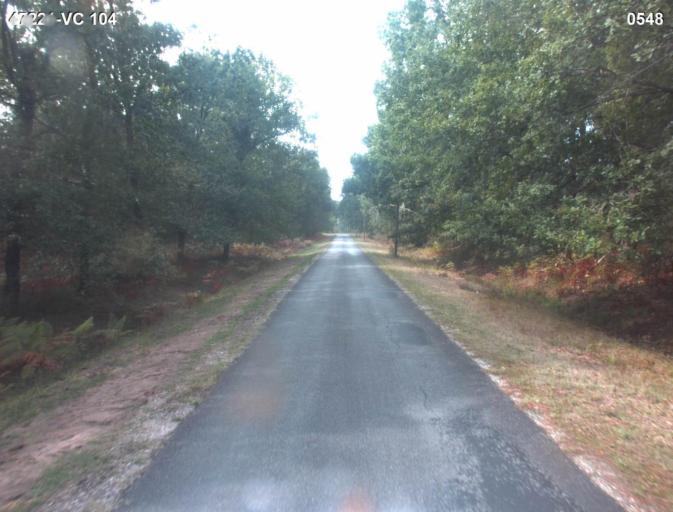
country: FR
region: Aquitaine
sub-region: Departement du Lot-et-Garonne
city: Mezin
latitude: 44.1238
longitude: 0.2215
